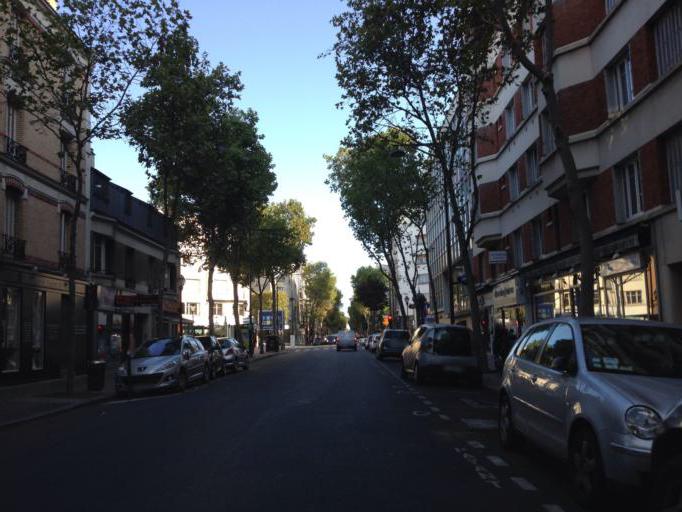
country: FR
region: Ile-de-France
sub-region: Departement des Hauts-de-Seine
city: Boulogne-Billancourt
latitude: 48.8281
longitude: 2.2467
